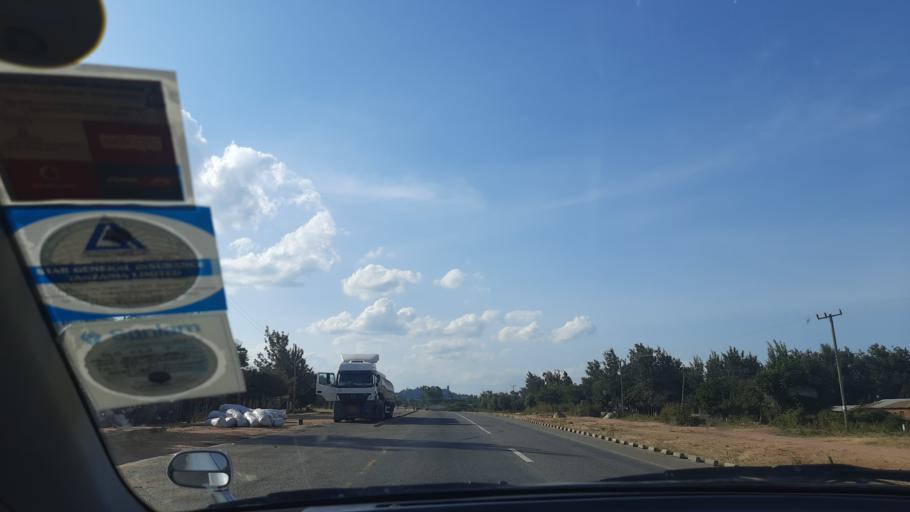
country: TZ
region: Singida
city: Puma
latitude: -5.0019
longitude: 34.7572
